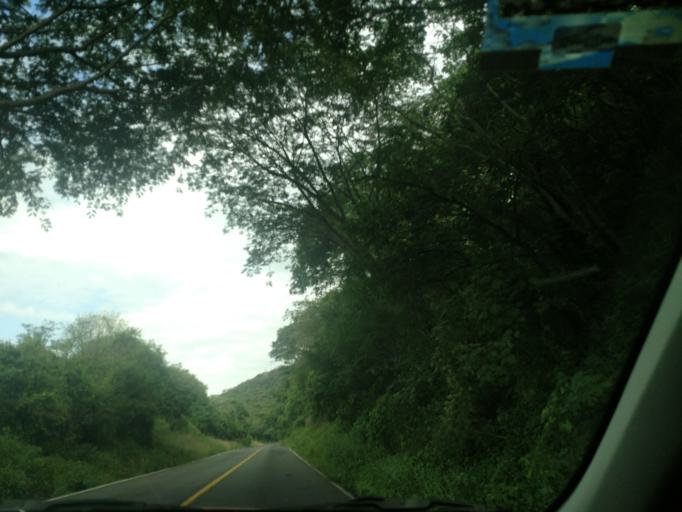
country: MX
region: Jalisco
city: Ameca
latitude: 20.5283
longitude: -104.2152
